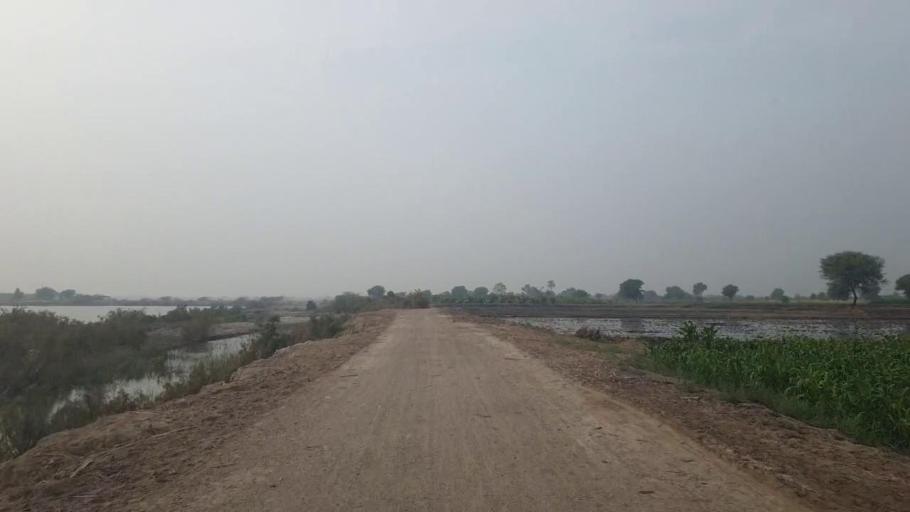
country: PK
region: Sindh
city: Berani
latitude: 25.8238
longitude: 68.7330
